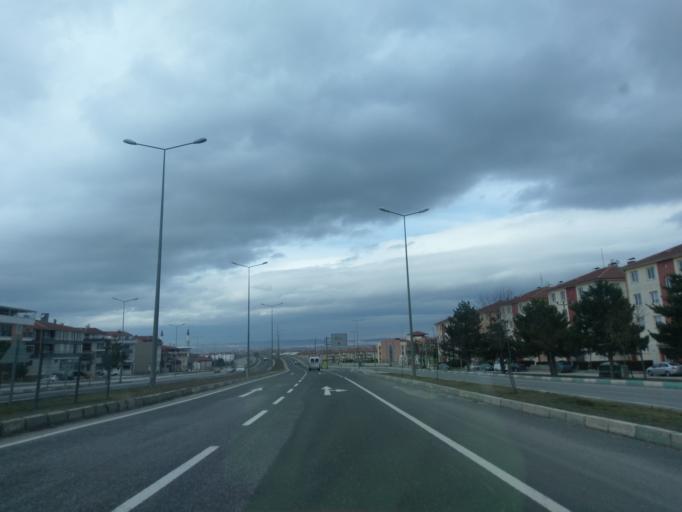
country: TR
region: Kuetahya
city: Kutahya
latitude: 39.4020
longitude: 30.0312
